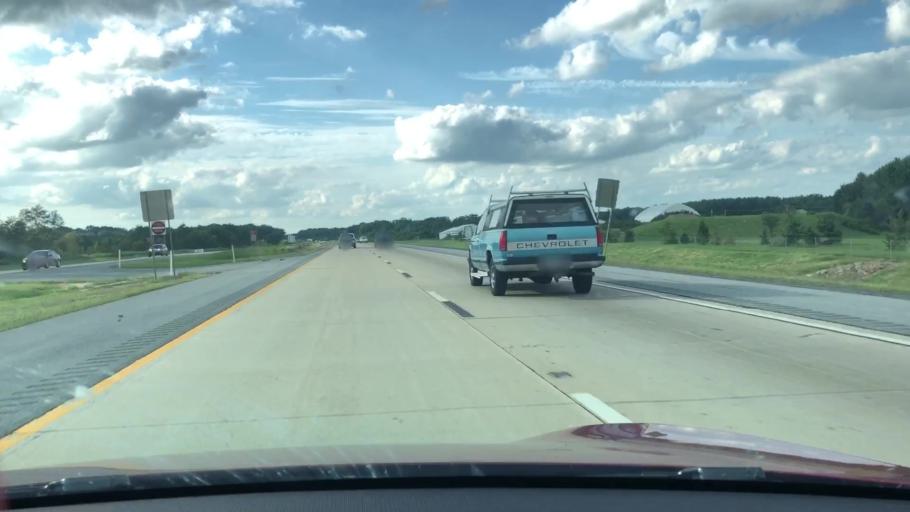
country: US
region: Delaware
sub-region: Kent County
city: Clayton
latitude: 39.3419
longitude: -75.6392
